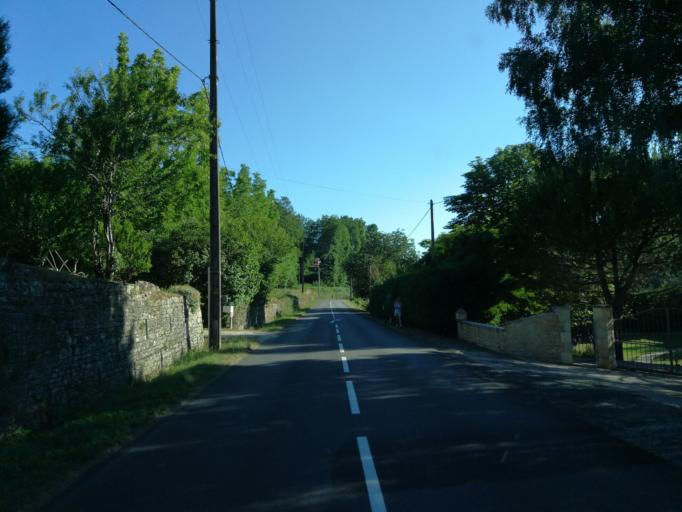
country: FR
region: Midi-Pyrenees
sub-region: Departement du Lot
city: Prayssac
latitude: 44.5890
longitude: 1.1704
